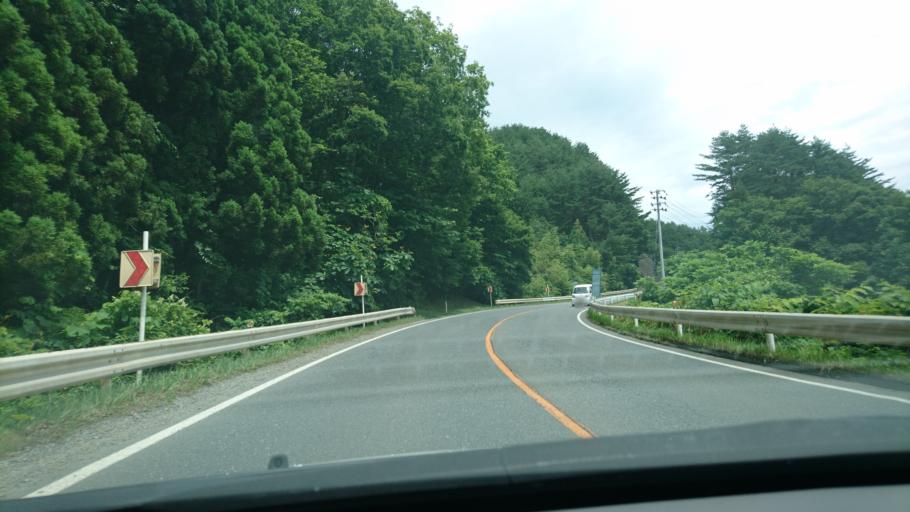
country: JP
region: Iwate
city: Miyako
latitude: 39.7046
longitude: 141.9585
